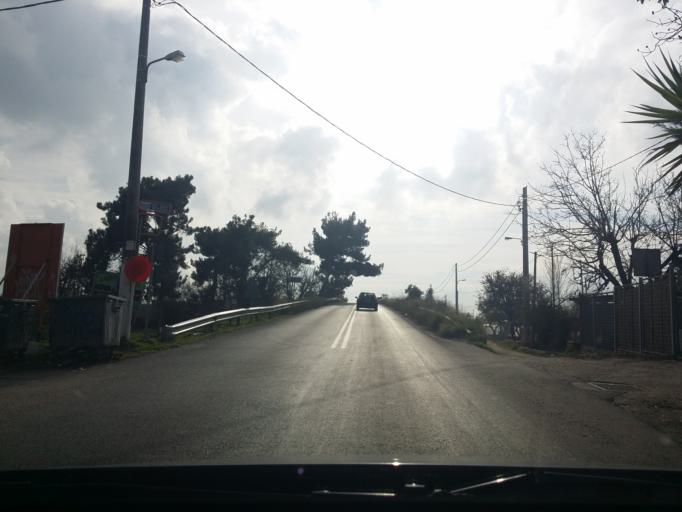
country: GR
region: Attica
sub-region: Nomarchia Anatolikis Attikis
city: Varybobi
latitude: 38.0999
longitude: 23.7791
